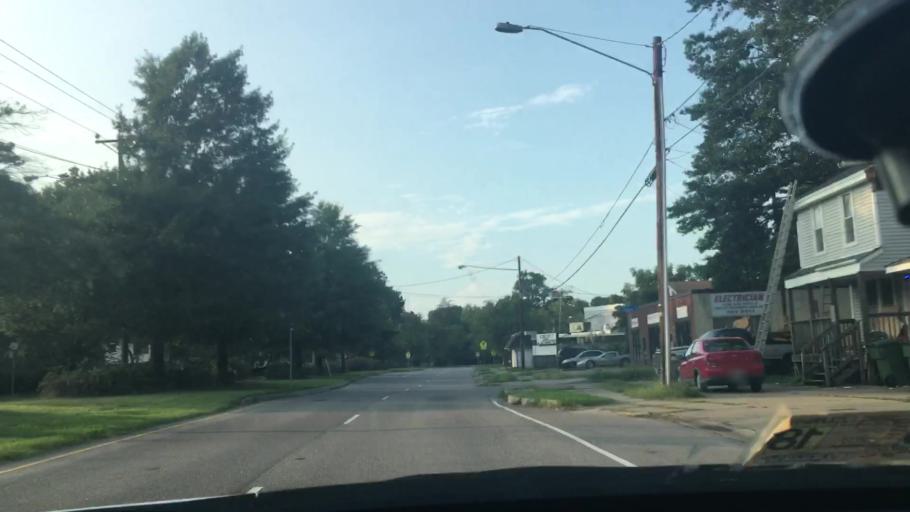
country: US
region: Virginia
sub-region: City of Norfolk
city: Norfolk
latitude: 36.9416
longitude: -76.2455
